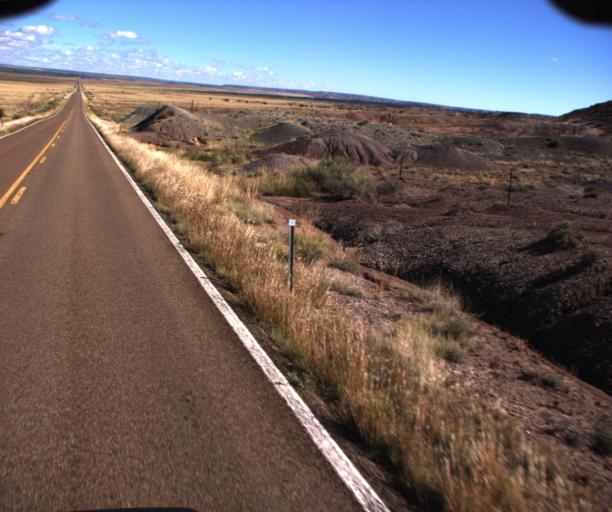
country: US
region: Arizona
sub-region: Apache County
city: Saint Johns
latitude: 34.6589
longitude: -109.2946
